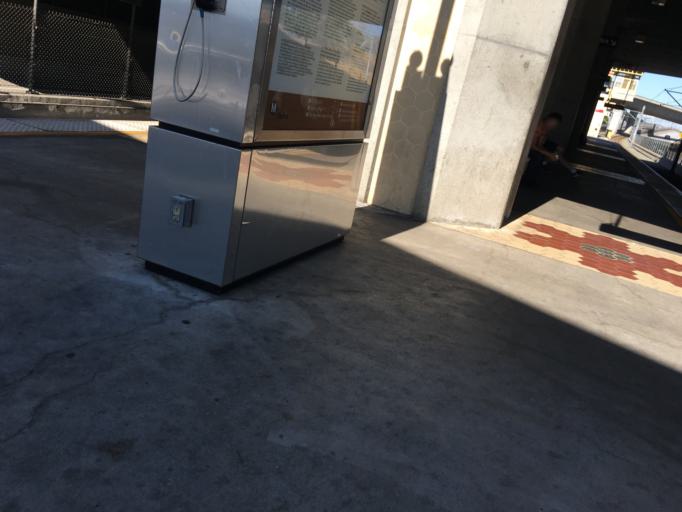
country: US
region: California
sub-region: Los Angeles County
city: Norwalk
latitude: 33.9141
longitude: -118.1044
